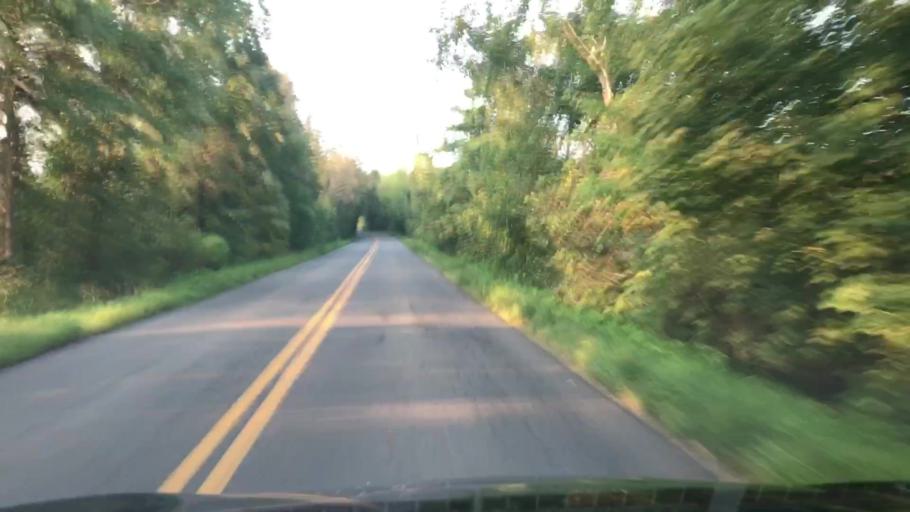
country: US
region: Virginia
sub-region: Prince William County
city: Nokesville
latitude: 38.6549
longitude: -77.6780
